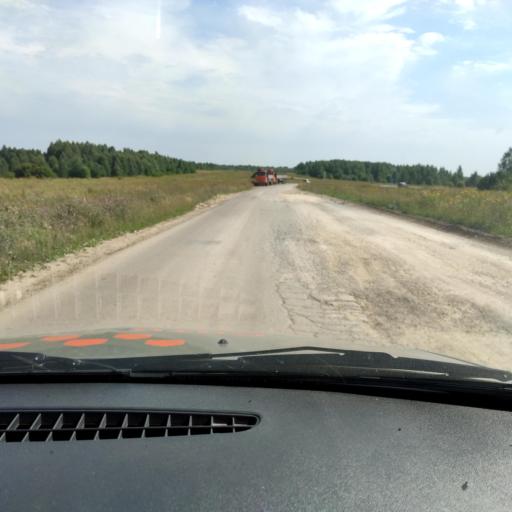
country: RU
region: Bashkortostan
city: Pavlovka
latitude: 55.3929
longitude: 56.4633
